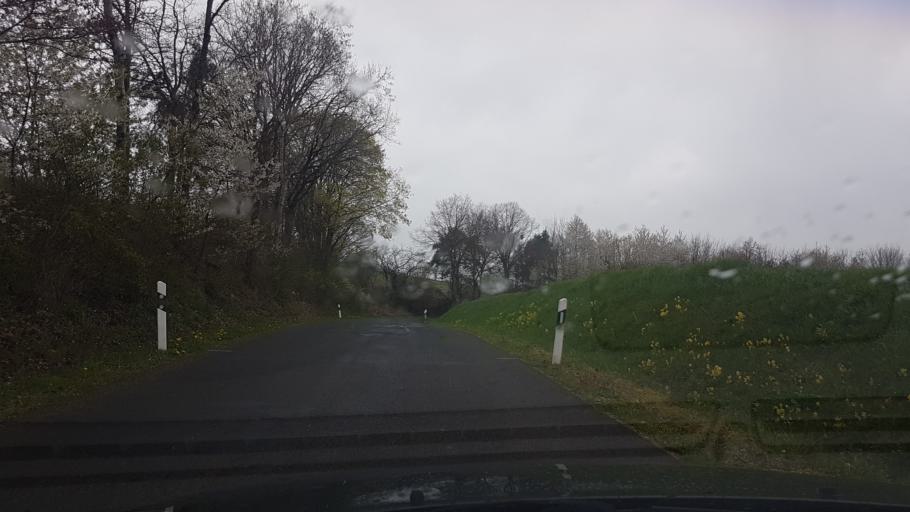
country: DE
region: Bavaria
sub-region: Upper Franconia
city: Reckendorf
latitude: 50.0285
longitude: 10.8419
